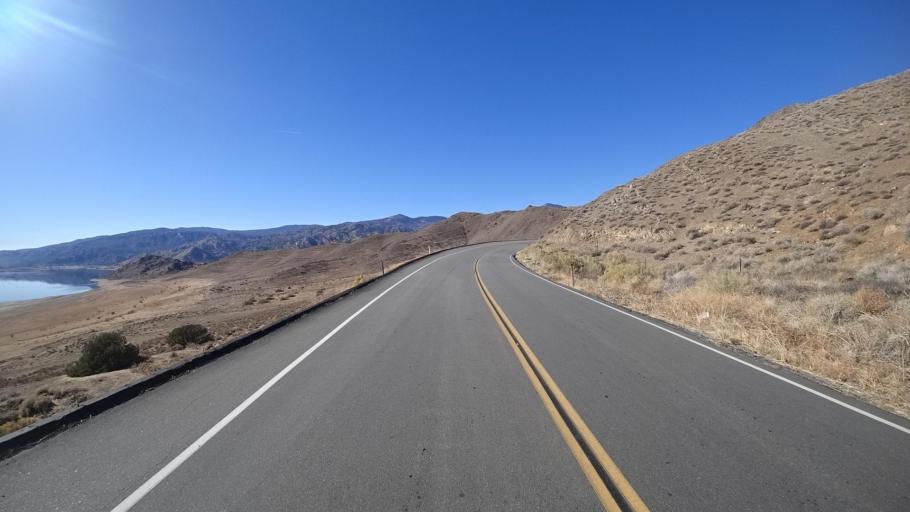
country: US
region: California
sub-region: Kern County
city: Wofford Heights
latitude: 35.6831
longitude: -118.4239
